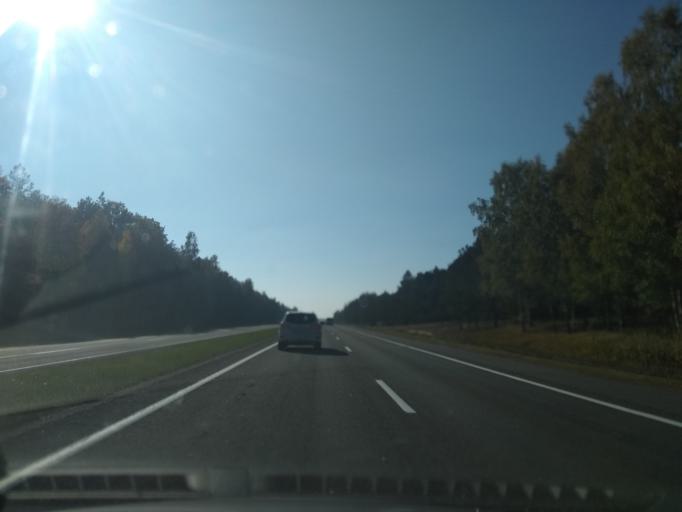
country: BY
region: Brest
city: Ivatsevichy
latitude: 52.7996
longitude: 25.5673
